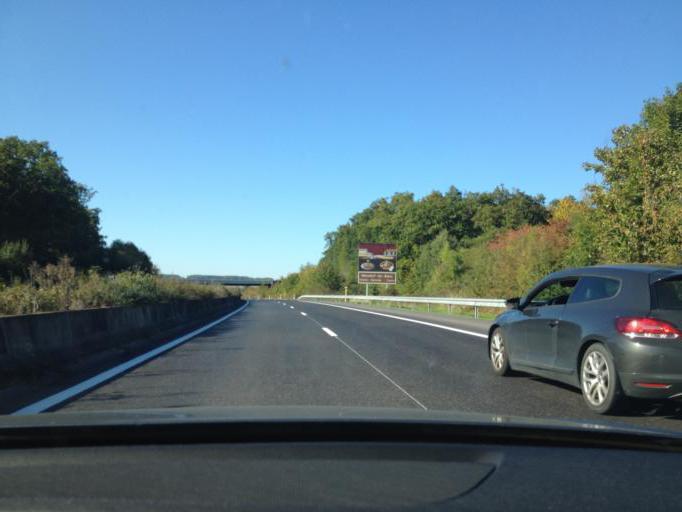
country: LU
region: Grevenmacher
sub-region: Canton de Remich
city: Mondorf-les-Bains
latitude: 49.5071
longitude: 6.3026
